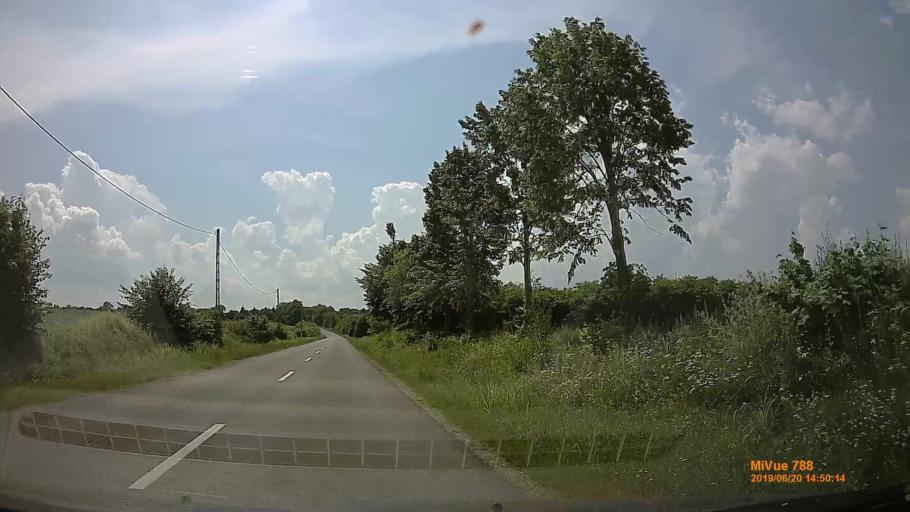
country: HU
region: Baranya
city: Kozarmisleny
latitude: 46.0149
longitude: 18.2668
